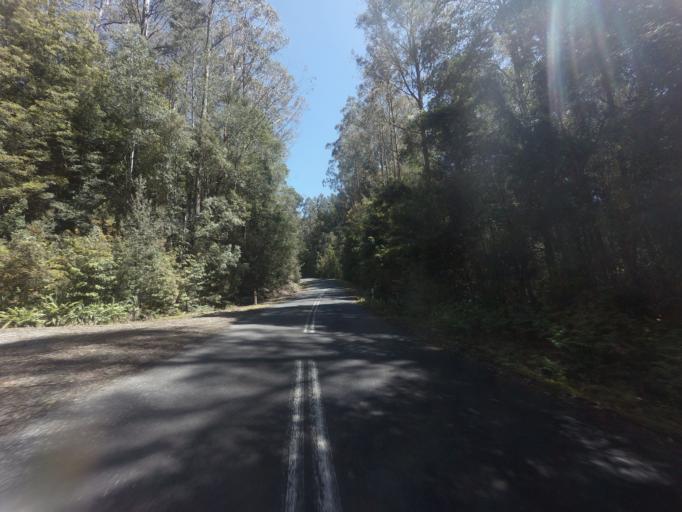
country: AU
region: Tasmania
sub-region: Huon Valley
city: Geeveston
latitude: -42.8283
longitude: 146.3213
